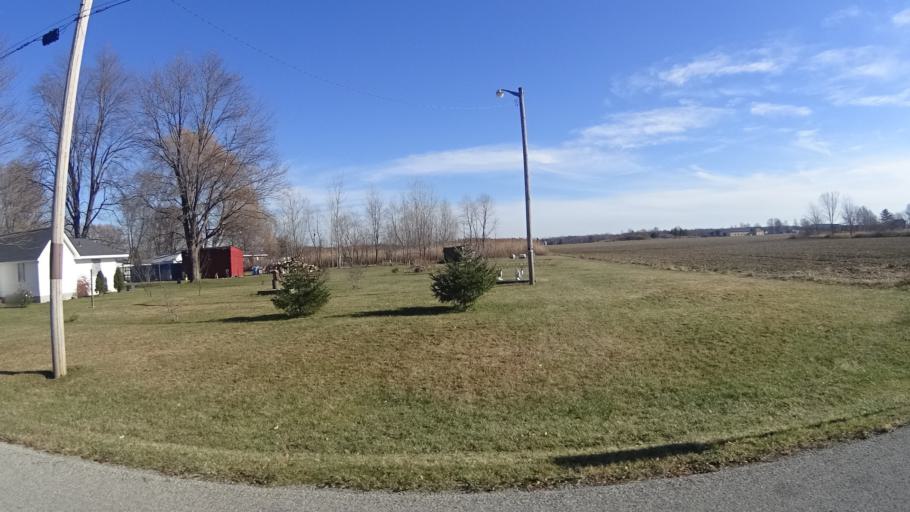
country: US
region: Ohio
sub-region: Lorain County
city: Camden
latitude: 41.2901
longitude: -82.2882
